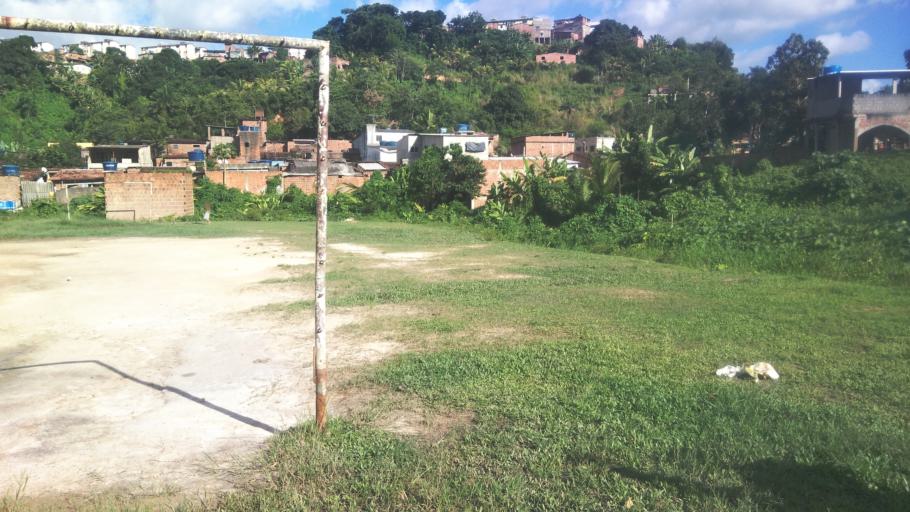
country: BR
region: Pernambuco
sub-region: Jaboatao Dos Guararapes
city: Jaboatao dos Guararapes
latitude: -8.0662
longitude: -35.0039
